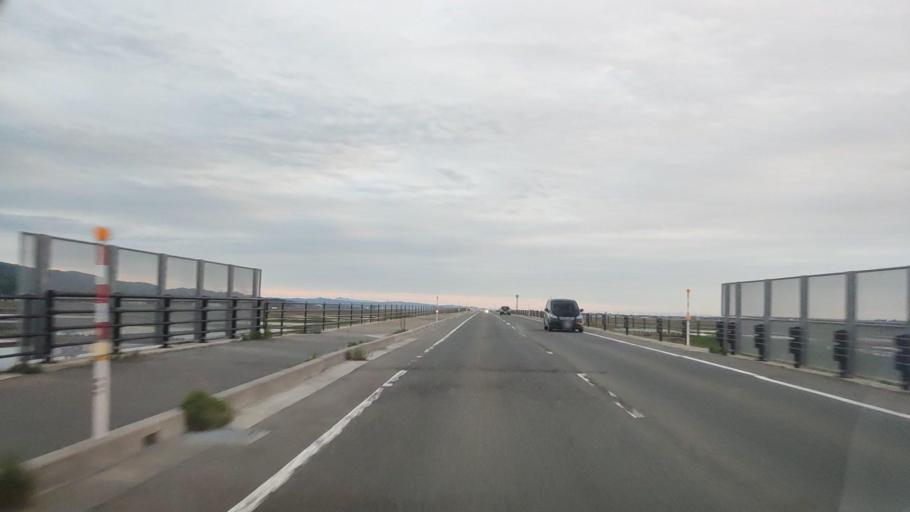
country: JP
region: Niigata
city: Niitsu-honcho
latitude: 37.7493
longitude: 139.0863
